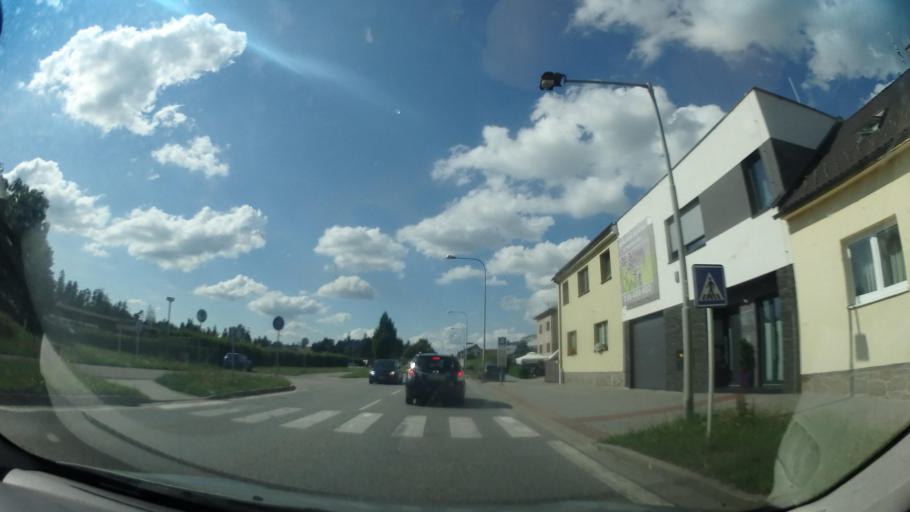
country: CZ
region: Vysocina
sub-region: Okres Zd'ar nad Sazavou
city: Zd'ar nad Sazavou
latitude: 49.5720
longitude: 15.9427
